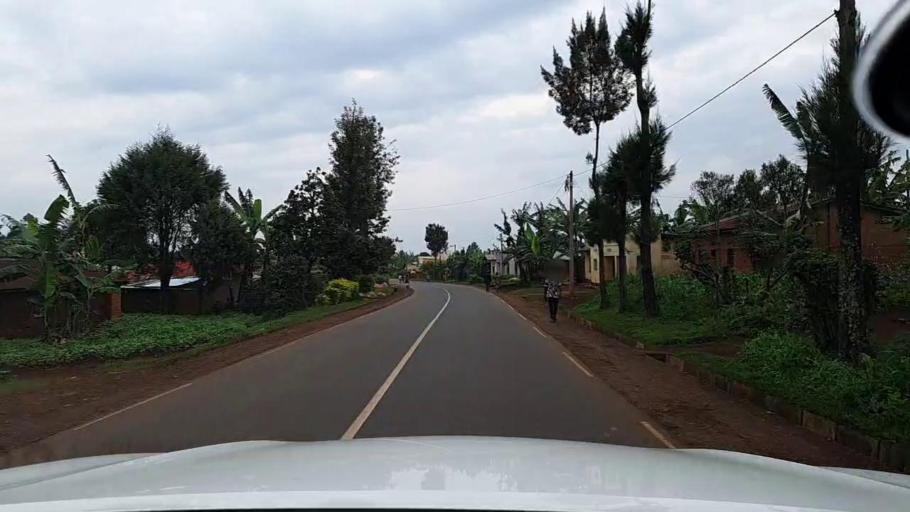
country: RW
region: Western Province
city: Cyangugu
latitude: -2.6030
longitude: 28.9331
